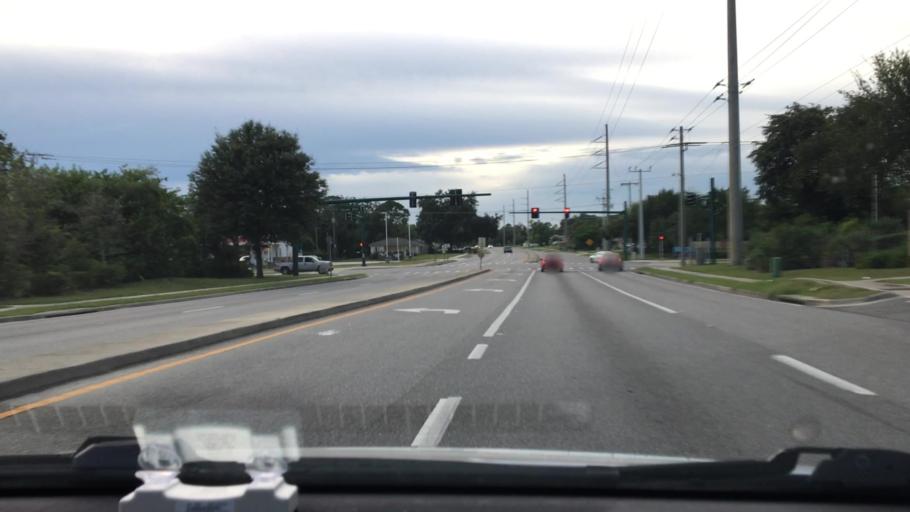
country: US
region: Florida
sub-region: Volusia County
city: Lake Helen
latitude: 28.9252
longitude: -81.1904
